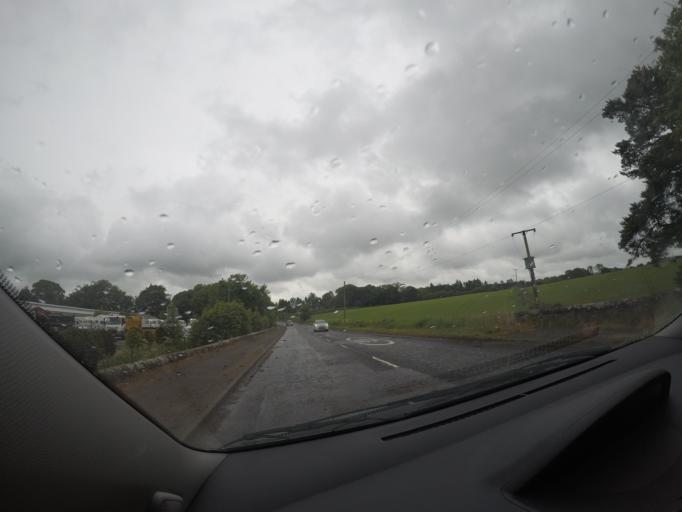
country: GB
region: Scotland
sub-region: Angus
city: Brechin
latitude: 56.7521
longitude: -2.6448
